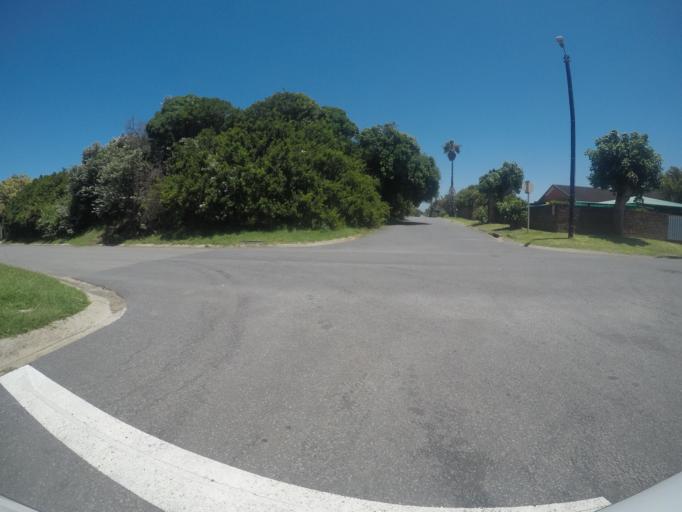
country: ZA
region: Eastern Cape
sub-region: Buffalo City Metropolitan Municipality
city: East London
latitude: -32.9470
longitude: 28.0199
